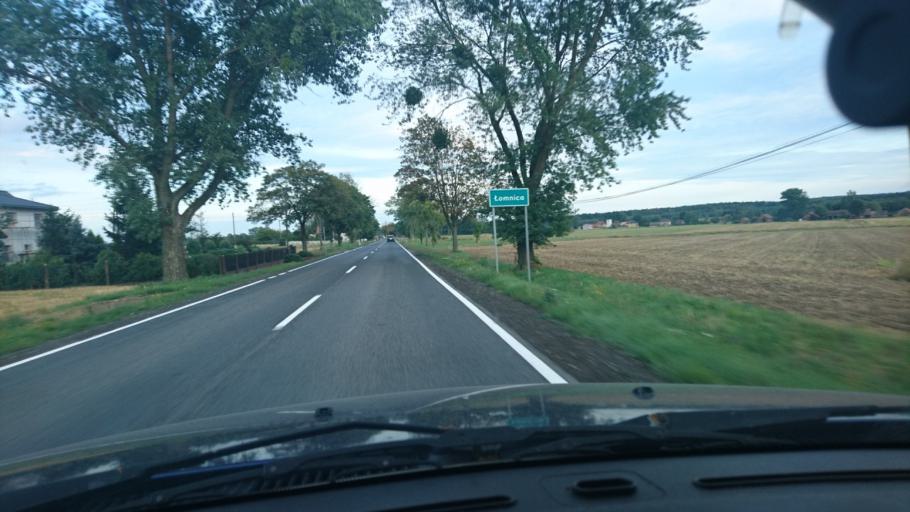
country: PL
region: Silesian Voivodeship
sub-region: Powiat lubliniecki
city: Sierakow Slaski
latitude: 50.8312
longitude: 18.5204
